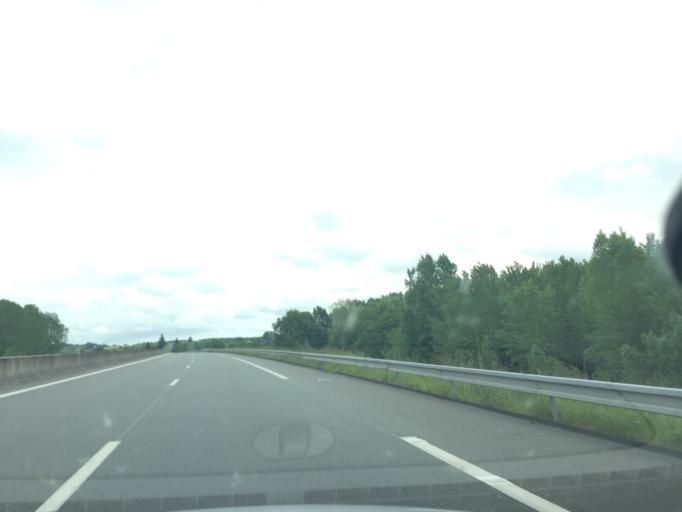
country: FR
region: Pays de la Loire
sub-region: Departement de la Sarthe
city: Chateau-du-Loir
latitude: 47.6624
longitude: 0.3829
